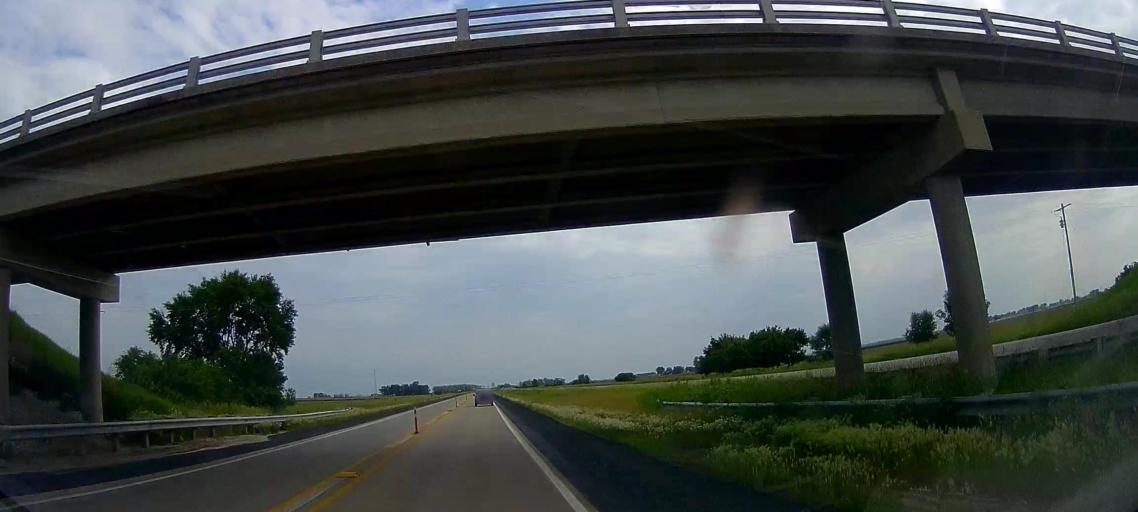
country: US
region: Nebraska
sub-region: Burt County
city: Tekamah
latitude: 41.7290
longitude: -96.0473
